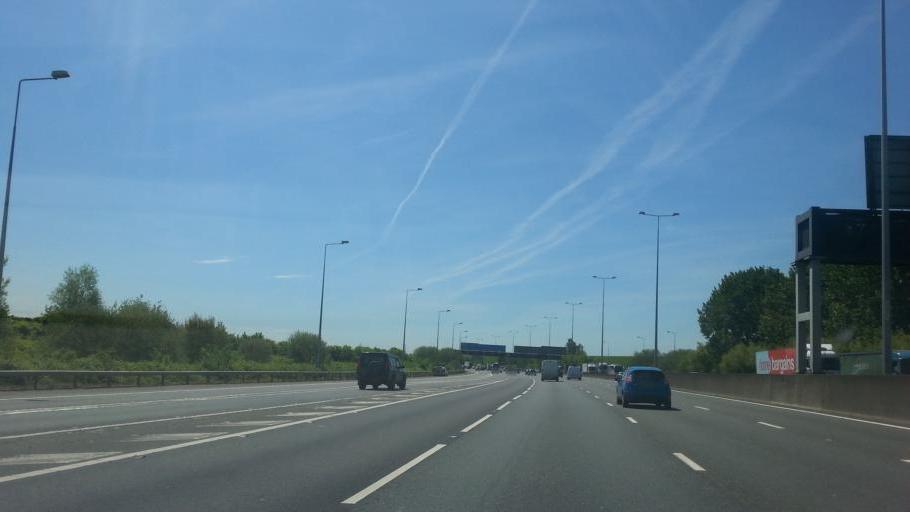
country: GB
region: England
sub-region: Surrey
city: Colnbrook
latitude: 51.4630
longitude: -0.5142
